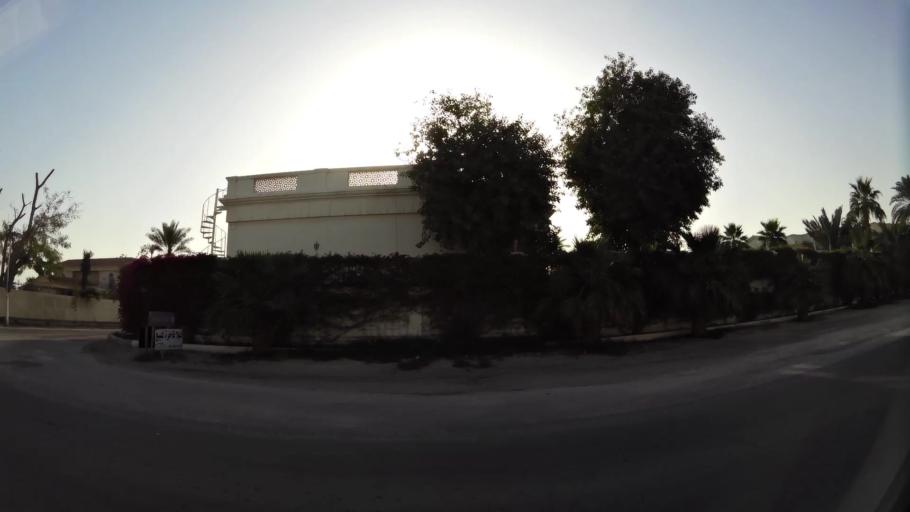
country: BH
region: Manama
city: Jidd Hafs
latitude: 26.2047
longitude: 50.4834
